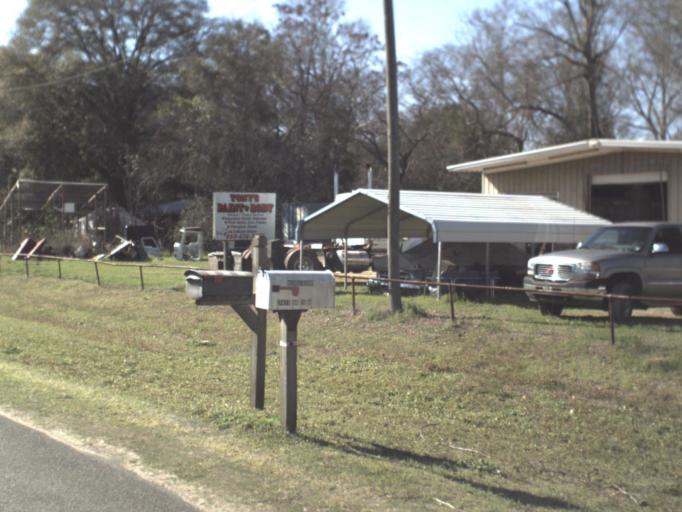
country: US
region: Florida
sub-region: Calhoun County
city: Blountstown
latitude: 30.4320
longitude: -85.0976
